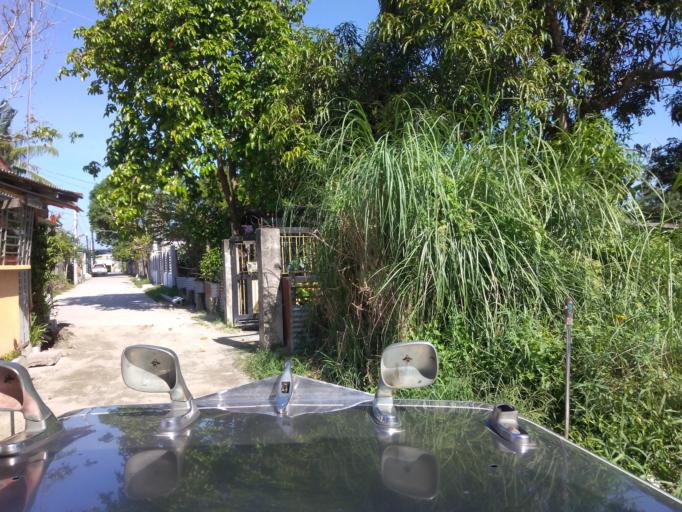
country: PH
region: Central Luzon
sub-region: Province of Pampanga
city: Mexico
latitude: 15.0714
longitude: 120.7236
